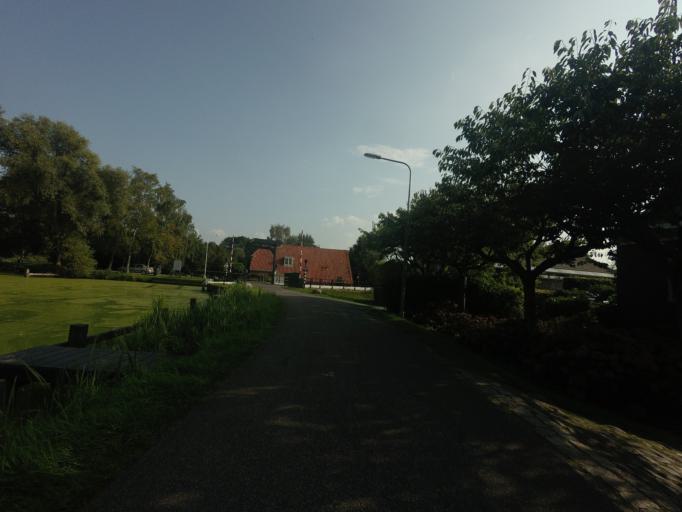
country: NL
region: Groningen
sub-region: Gemeente Haren
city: Haren
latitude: 53.1774
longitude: 6.5765
